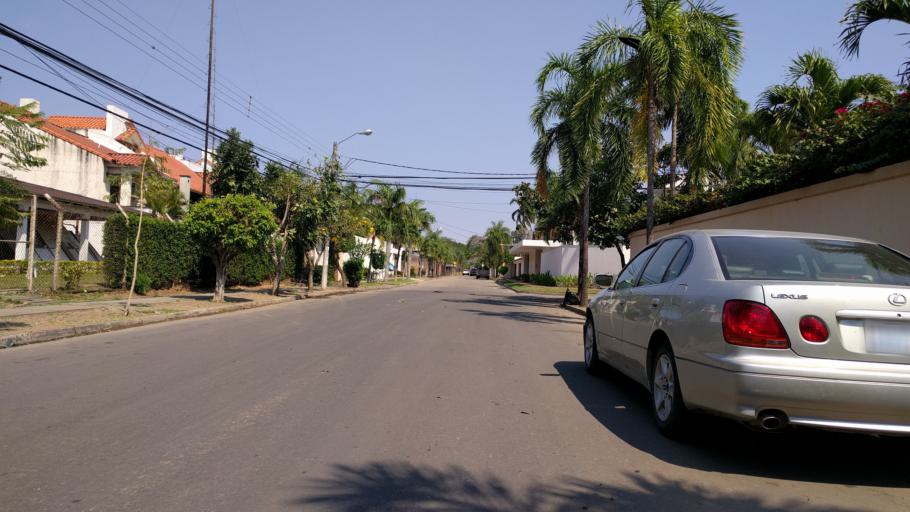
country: BO
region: Santa Cruz
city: Santa Cruz de la Sierra
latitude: -17.8036
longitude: -63.2020
